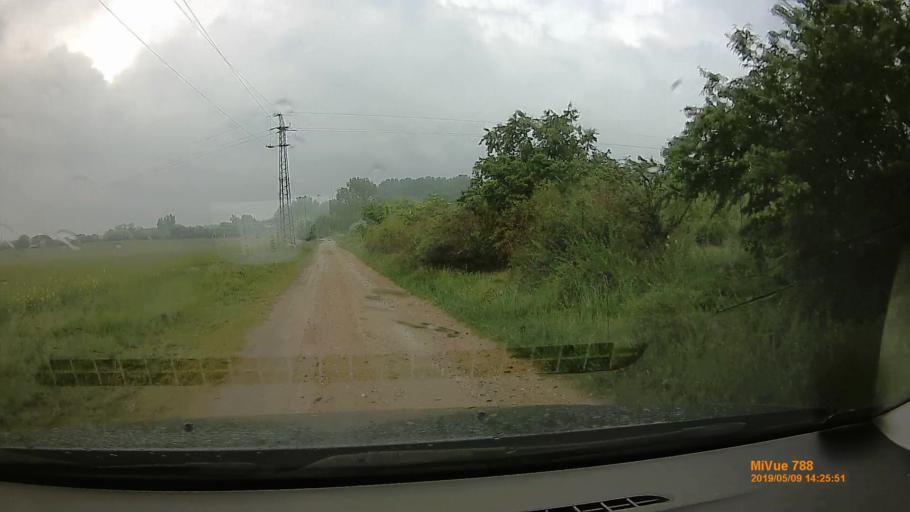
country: HU
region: Budapest
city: Budapest XVII. keruelet
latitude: 47.4958
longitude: 19.2171
